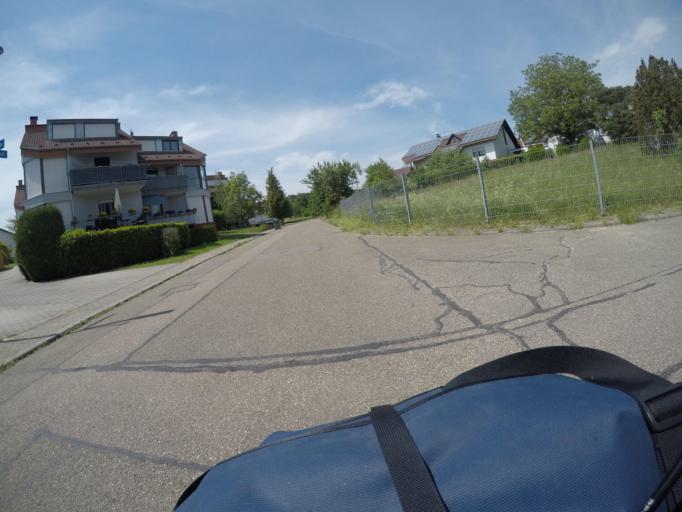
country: DE
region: Baden-Wuerttemberg
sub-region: Karlsruhe Region
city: Konigsbach-Stein
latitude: 48.9656
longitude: 8.5435
